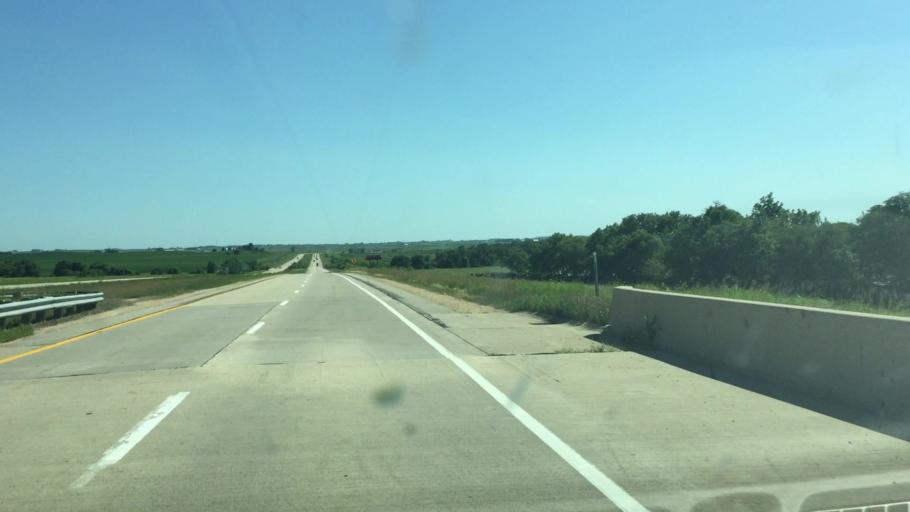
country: US
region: Iowa
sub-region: Jones County
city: Monticello
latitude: 42.2303
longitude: -91.1713
